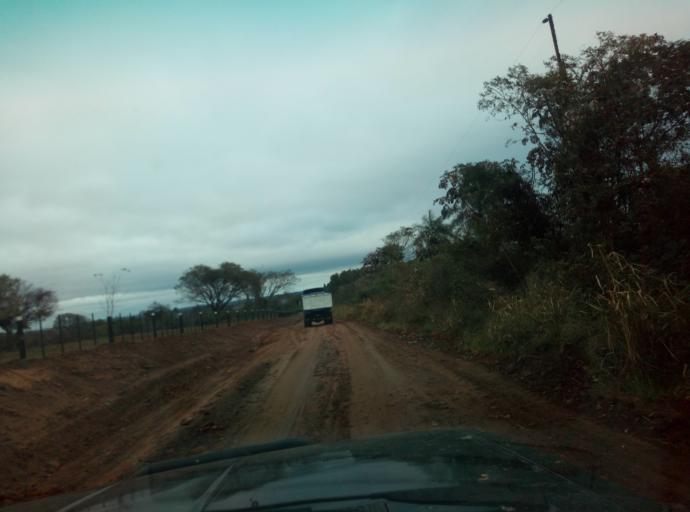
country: PY
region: Caaguazu
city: Carayao
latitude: -25.1902
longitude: -56.3824
